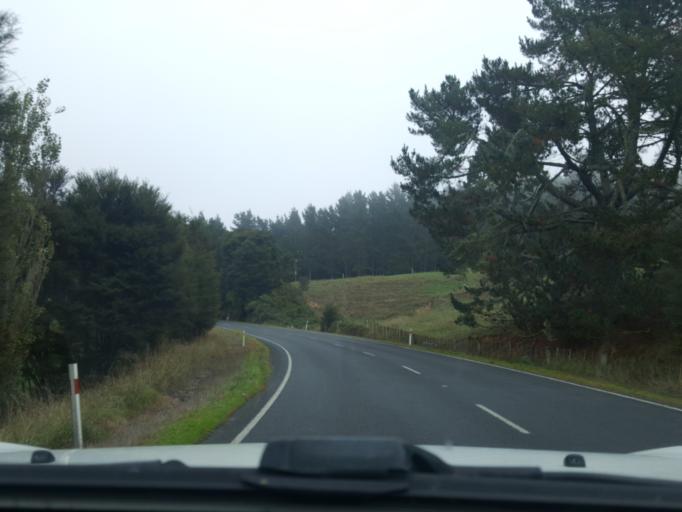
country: NZ
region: Auckland
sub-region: Auckland
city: Pukekohe East
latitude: -37.2871
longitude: 175.0396
